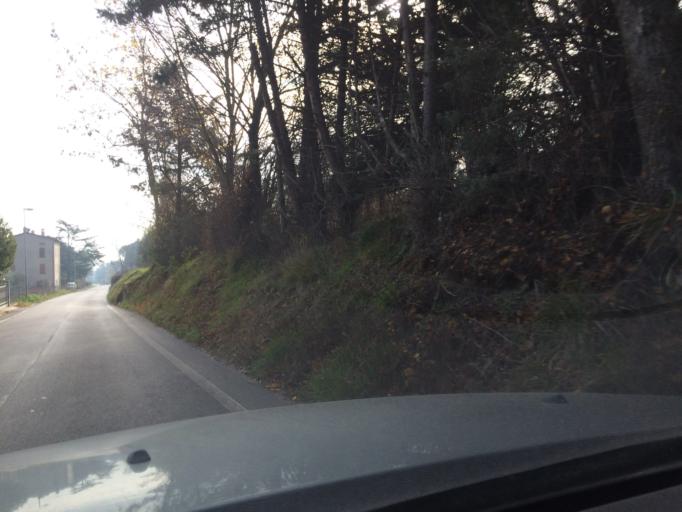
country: IT
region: Umbria
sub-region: Provincia di Perugia
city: Via Lippia
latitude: 43.1001
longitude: 12.4901
